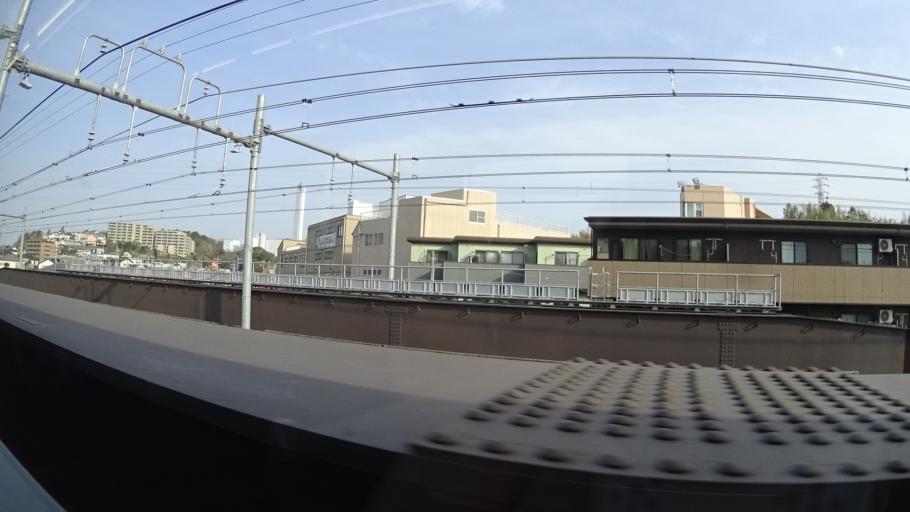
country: JP
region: Kanagawa
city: Yokohama
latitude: 35.4779
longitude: 139.5612
